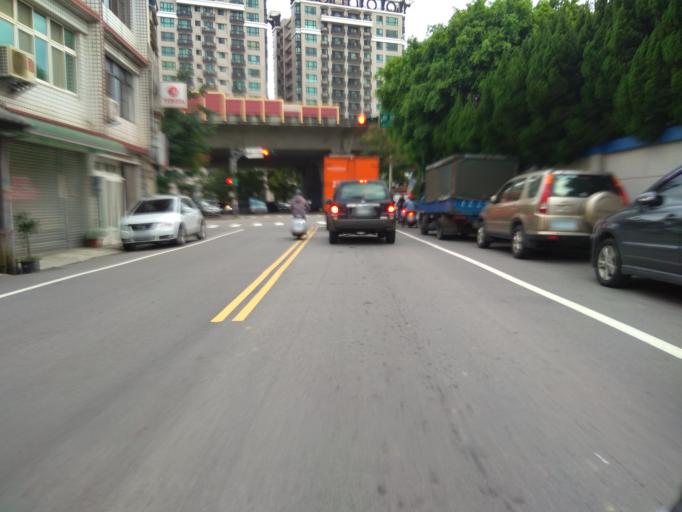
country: TW
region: Taiwan
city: Daxi
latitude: 24.8607
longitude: 121.2157
